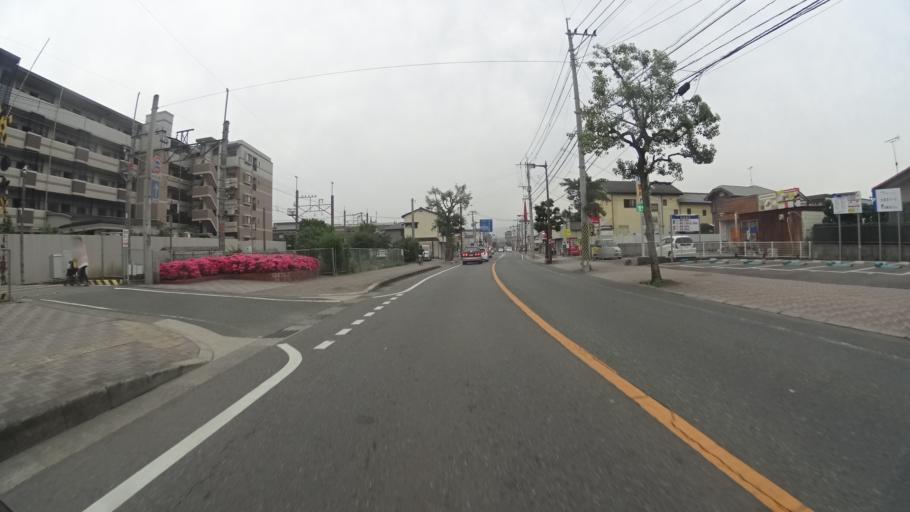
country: JP
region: Fukuoka
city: Dazaifu
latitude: 33.5177
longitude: 130.5307
